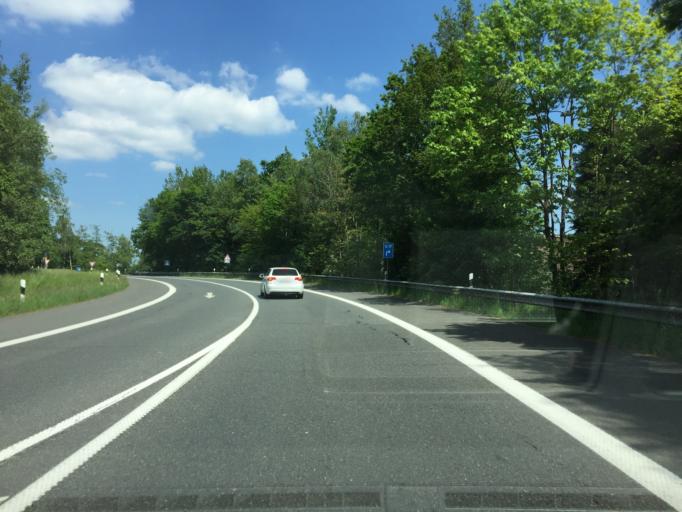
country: DE
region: Lower Saxony
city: Rastede
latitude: 53.2423
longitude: 8.1782
